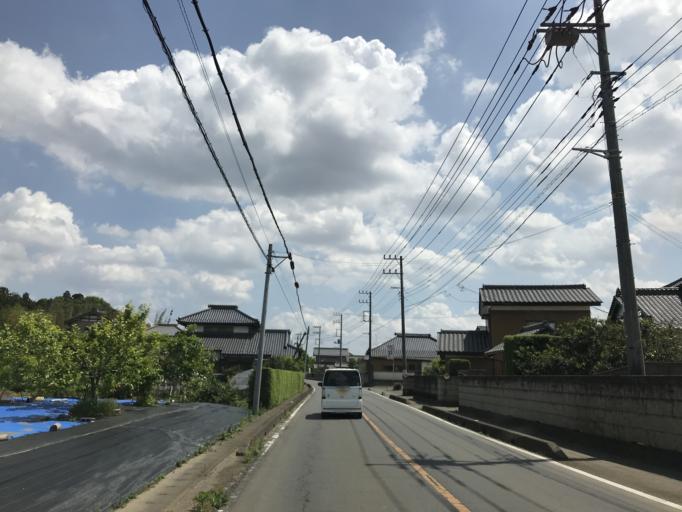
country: JP
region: Ibaraki
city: Mitsukaido
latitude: 36.0538
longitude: 140.0383
